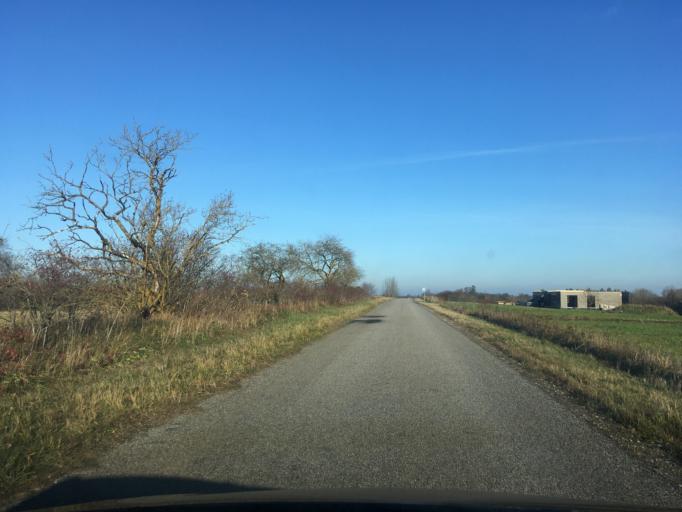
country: EE
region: Harju
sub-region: Maardu linn
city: Maardu
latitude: 59.4671
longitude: 25.1105
